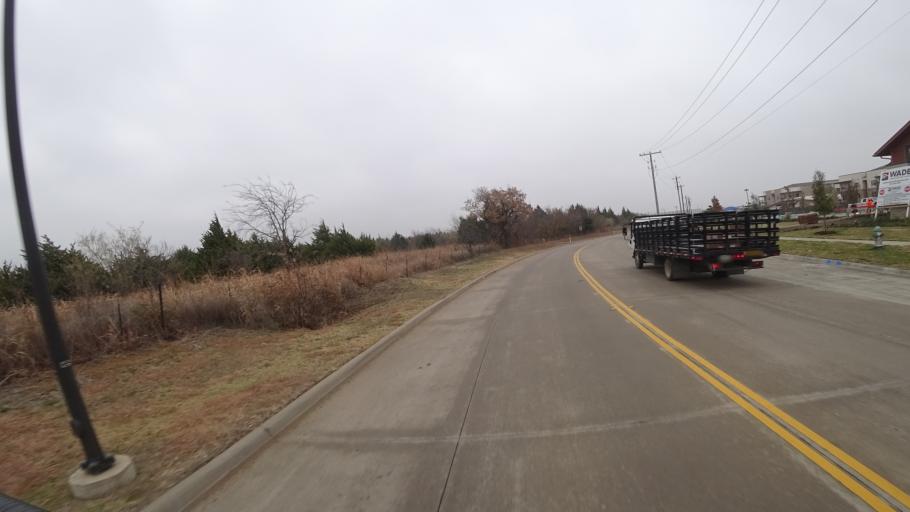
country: US
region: Texas
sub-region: Denton County
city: The Colony
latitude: 33.0650
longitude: -96.9116
